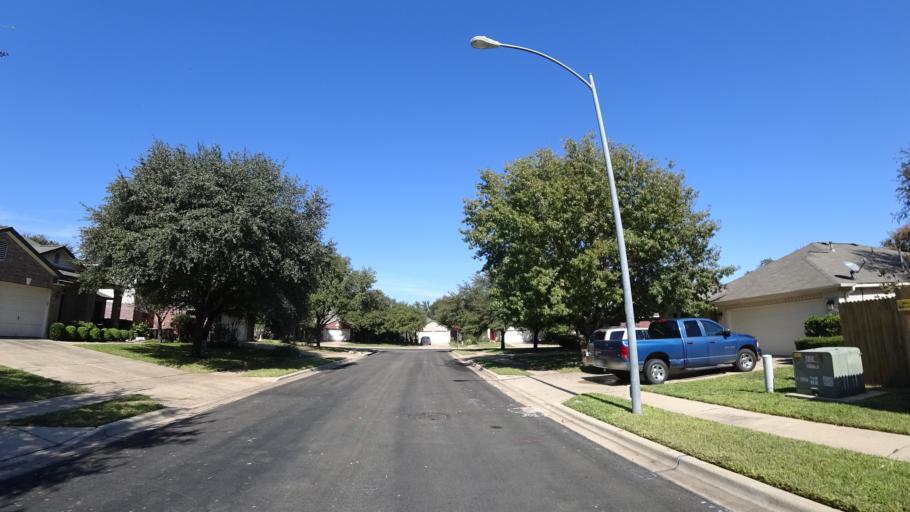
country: US
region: Texas
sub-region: Travis County
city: Shady Hollow
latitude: 30.1970
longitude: -97.8631
